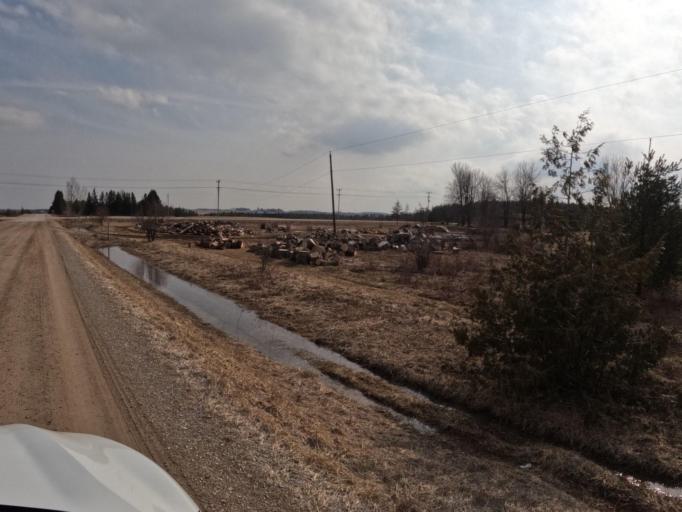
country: CA
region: Ontario
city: Orangeville
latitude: 43.9090
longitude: -80.2869
